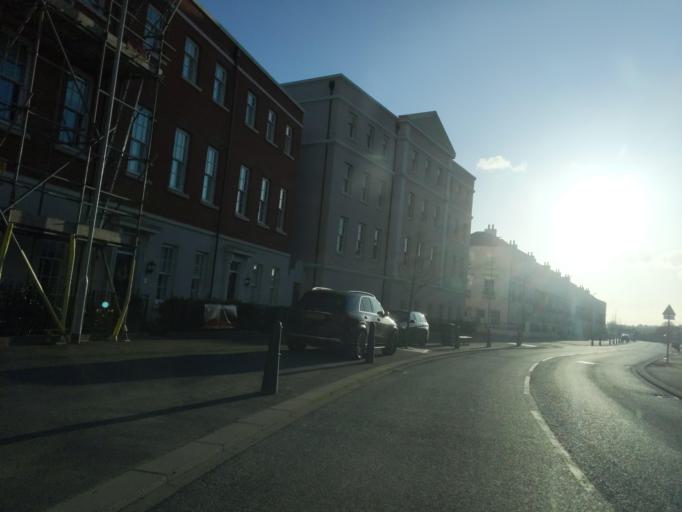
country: GB
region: England
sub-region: Devon
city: Plympton
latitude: 50.3656
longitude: -4.0522
